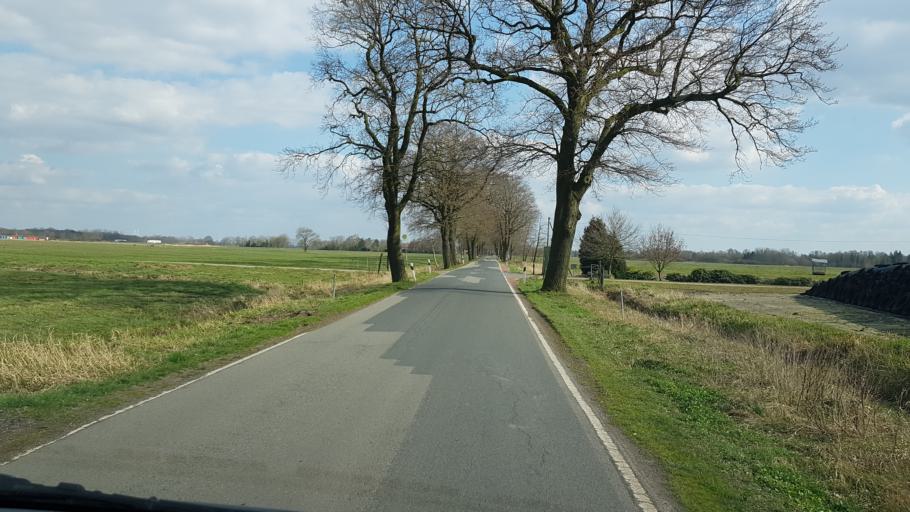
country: DE
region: Lower Saxony
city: Rastede
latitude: 53.2598
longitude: 8.2898
